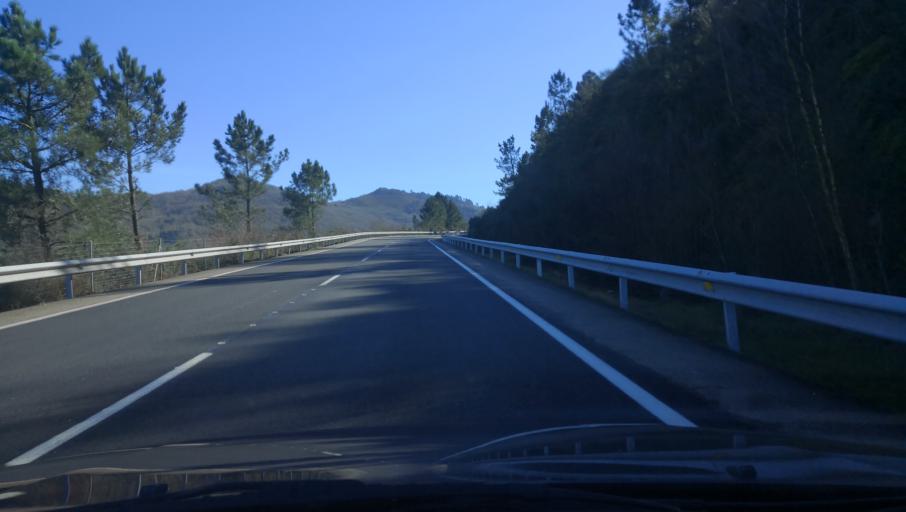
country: ES
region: Galicia
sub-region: Provincia de Ourense
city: Allariz
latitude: 42.1884
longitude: -7.7682
